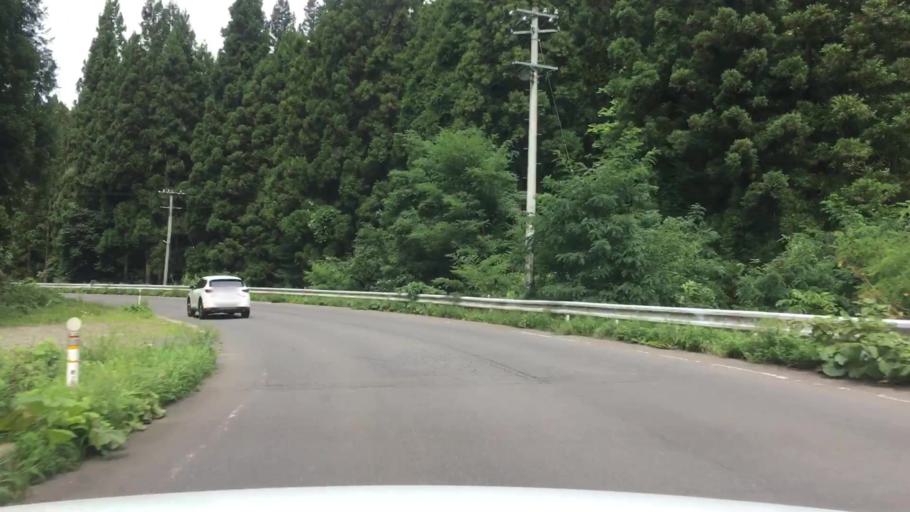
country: JP
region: Aomori
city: Shimokizukuri
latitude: 40.7357
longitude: 140.2502
